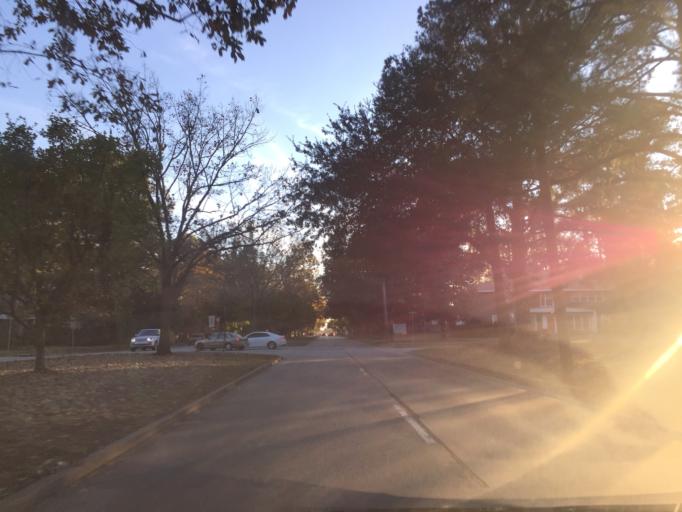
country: US
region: Georgia
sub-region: Chatham County
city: Savannah
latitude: 32.0328
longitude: -81.1066
